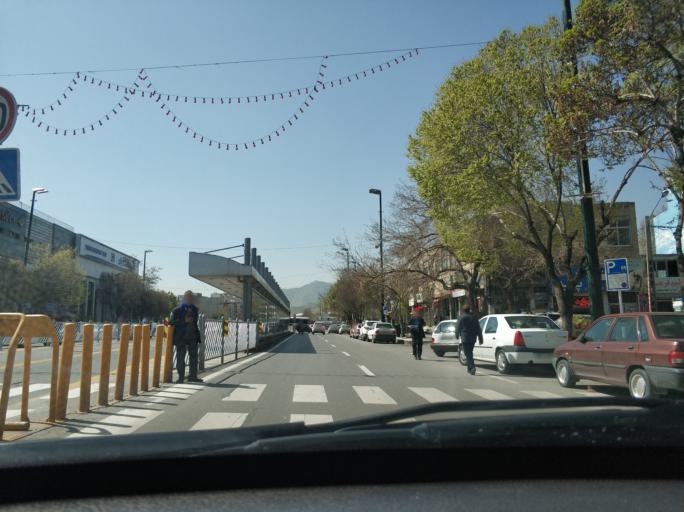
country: IR
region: Razavi Khorasan
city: Mashhad
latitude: 36.2695
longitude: 59.5997
